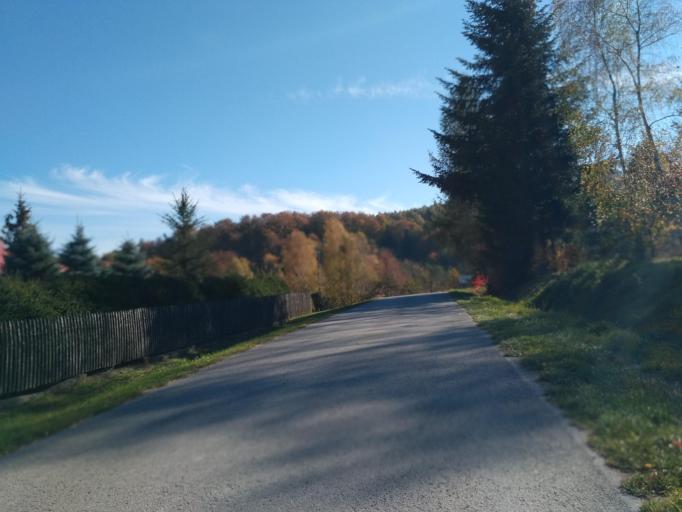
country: PL
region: Subcarpathian Voivodeship
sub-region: Powiat ropczycko-sedziszowski
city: Iwierzyce
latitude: 49.9782
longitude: 21.7283
